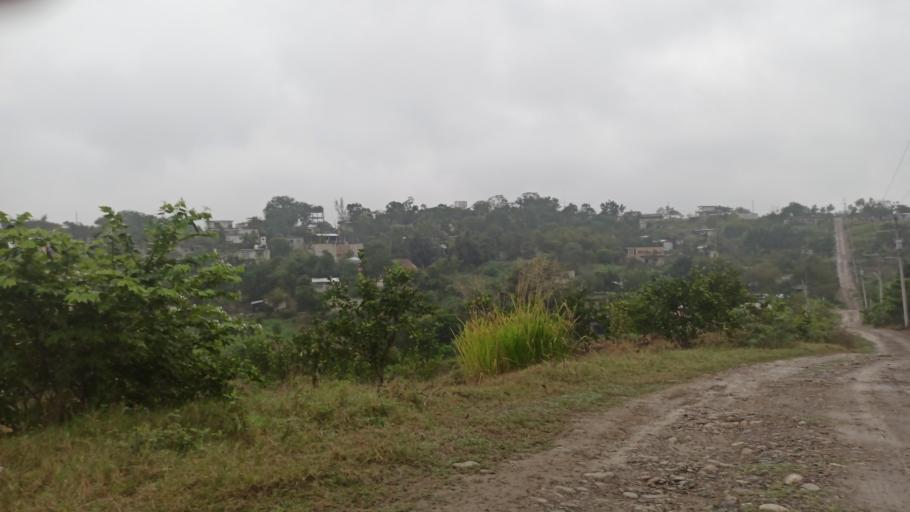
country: MX
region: Veracruz
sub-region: Papantla
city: El Chote
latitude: 20.3609
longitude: -97.3414
